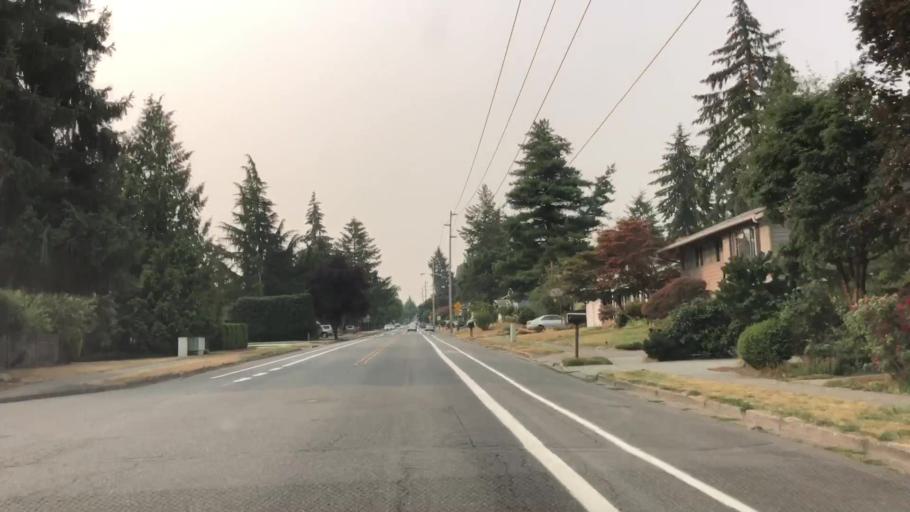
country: US
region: Washington
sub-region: King County
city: Redmond
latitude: 47.6586
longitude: -122.1326
